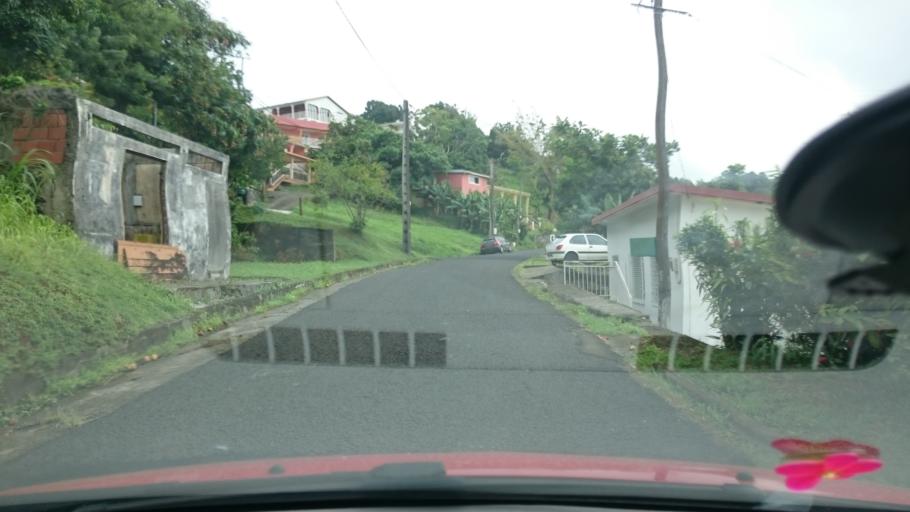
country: MQ
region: Martinique
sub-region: Martinique
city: Sainte-Luce
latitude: 14.4921
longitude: -60.9248
